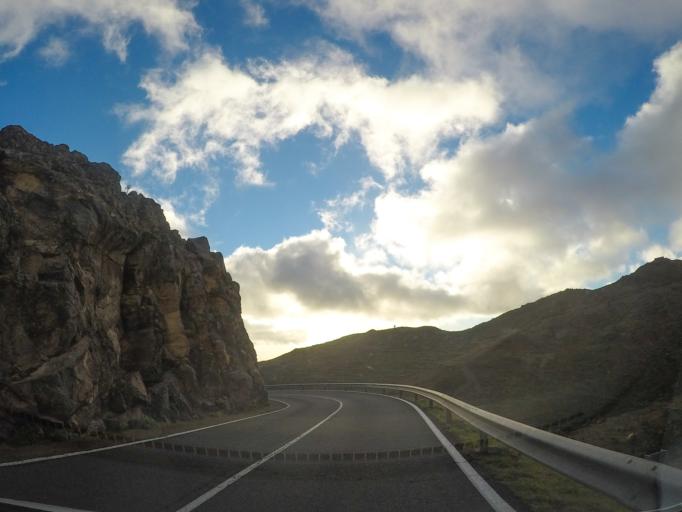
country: ES
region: Canary Islands
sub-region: Provincia de Santa Cruz de Tenerife
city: Alajero
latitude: 28.0832
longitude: -17.2455
